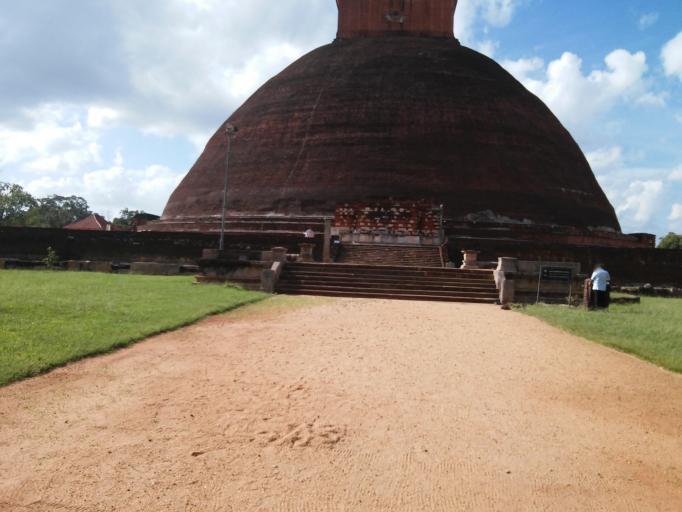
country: LK
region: North Central
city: Anuradhapura
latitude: 8.3503
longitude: 80.4035
